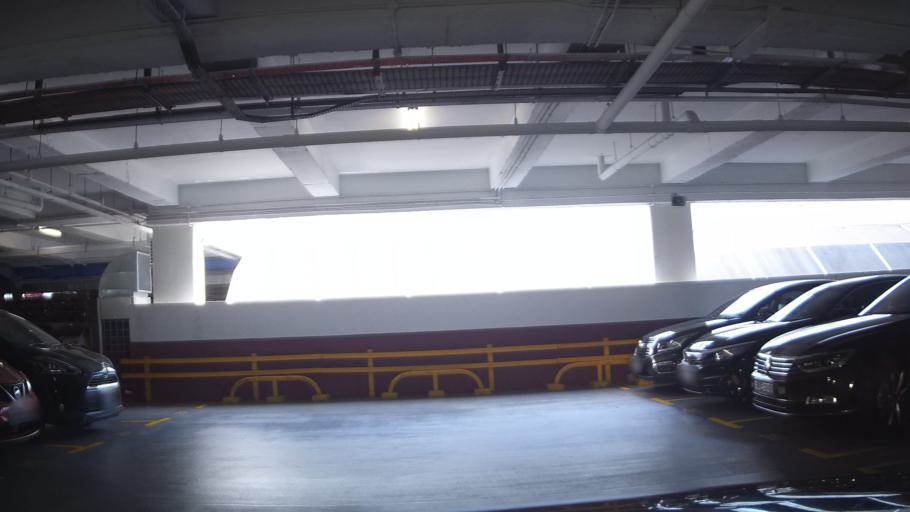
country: SG
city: Singapore
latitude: 1.2228
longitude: 103.8541
